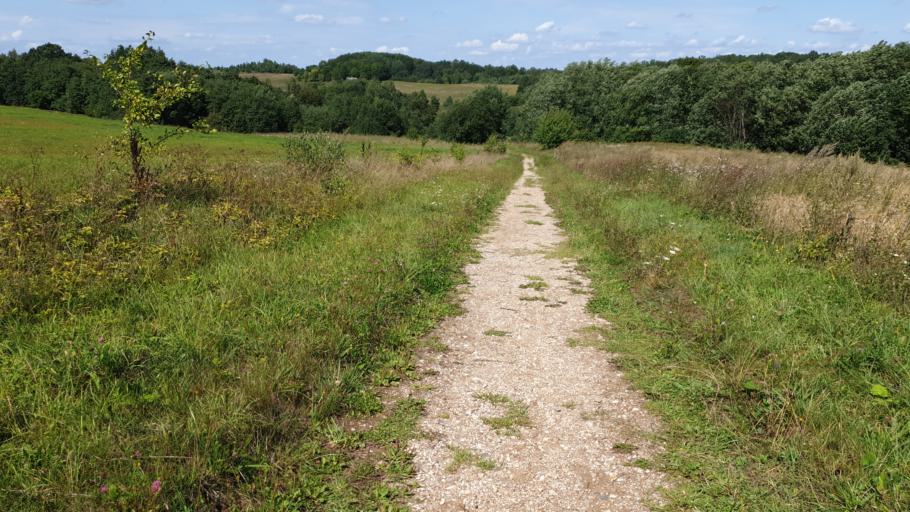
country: LT
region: Vilnius County
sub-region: Vilniaus Rajonas
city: Vievis
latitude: 54.8219
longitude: 24.9458
